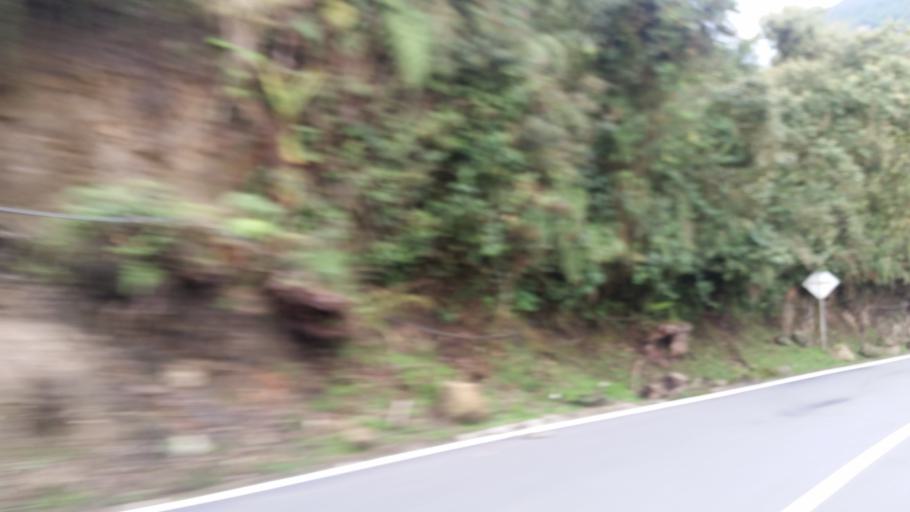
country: CO
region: Cundinamarca
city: Choachi
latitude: 4.5589
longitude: -73.9589
